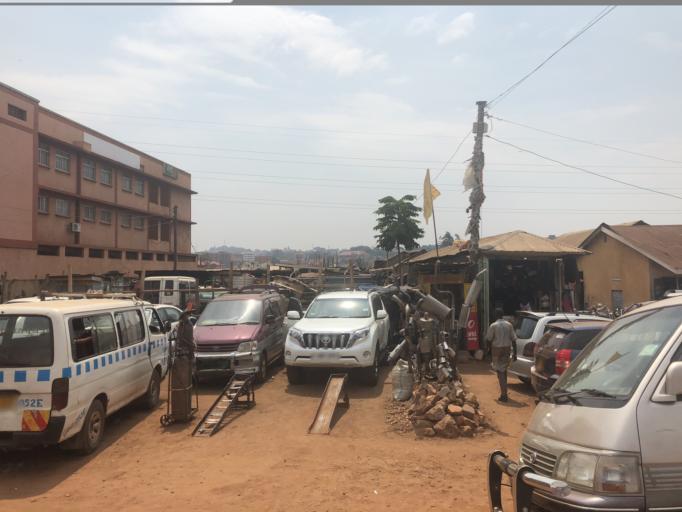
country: UG
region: Central Region
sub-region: Kampala District
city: Kampala
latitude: 0.2925
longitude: 32.5682
